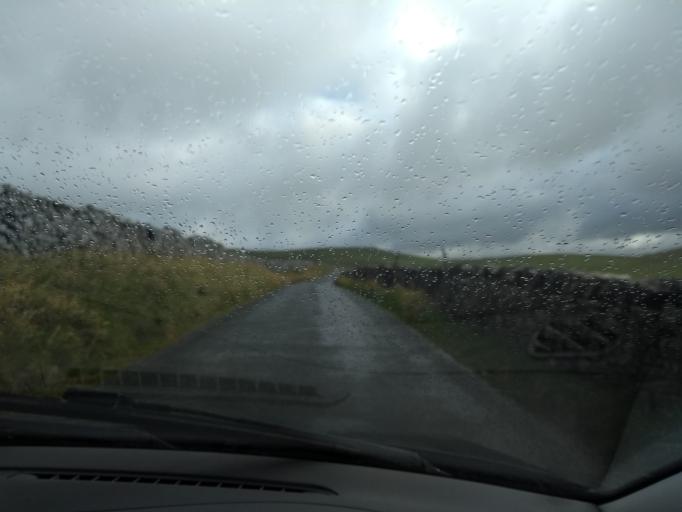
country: GB
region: England
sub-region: North Yorkshire
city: Settle
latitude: 54.1010
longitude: -2.2200
